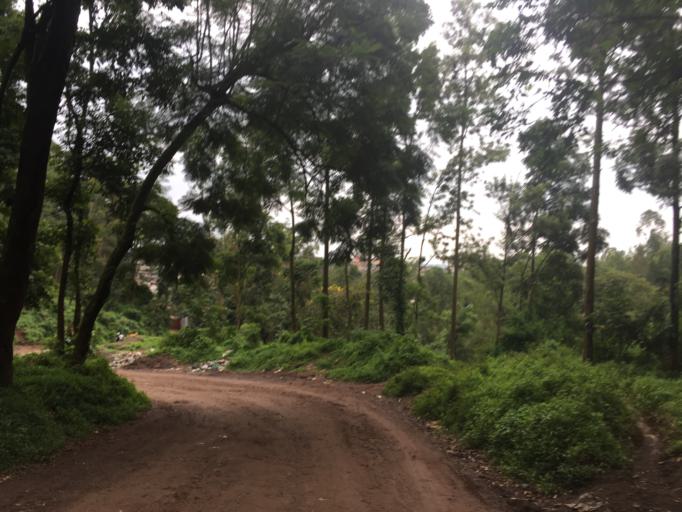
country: CD
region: South Kivu
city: Bukavu
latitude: -2.5028
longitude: 28.8478
